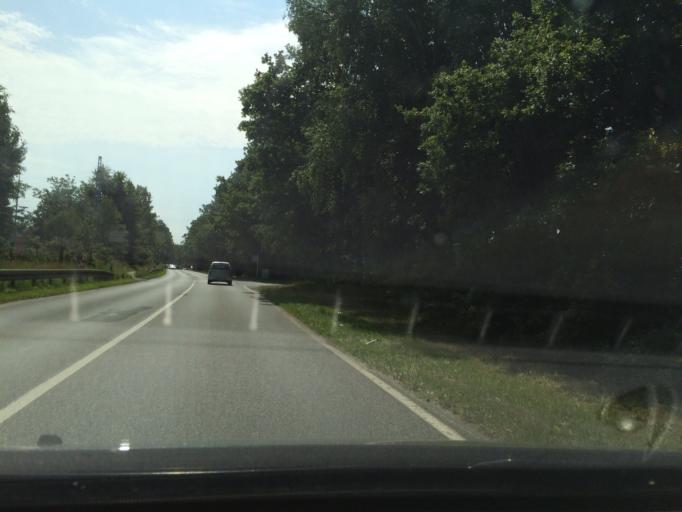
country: DE
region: Mecklenburg-Vorpommern
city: Ostseebad Binz
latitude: 54.4077
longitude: 13.5969
